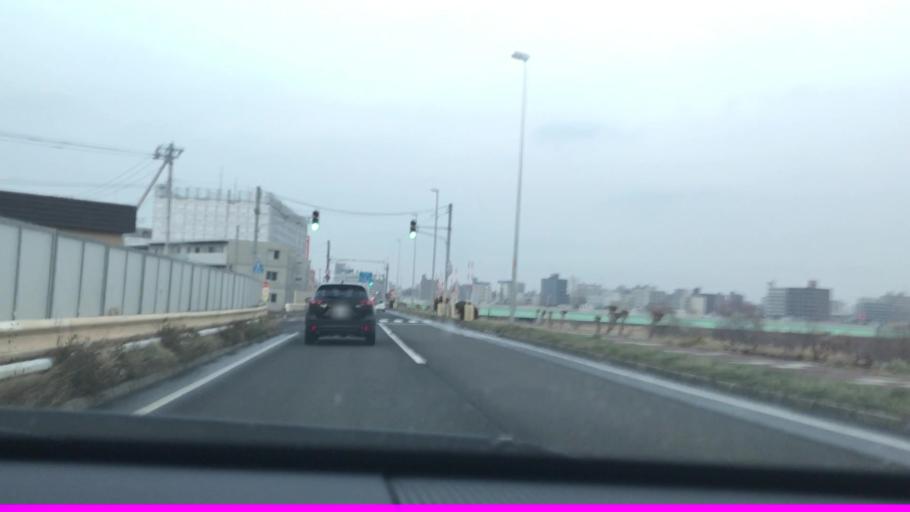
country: JP
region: Hokkaido
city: Sapporo
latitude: 43.0281
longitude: 141.3521
